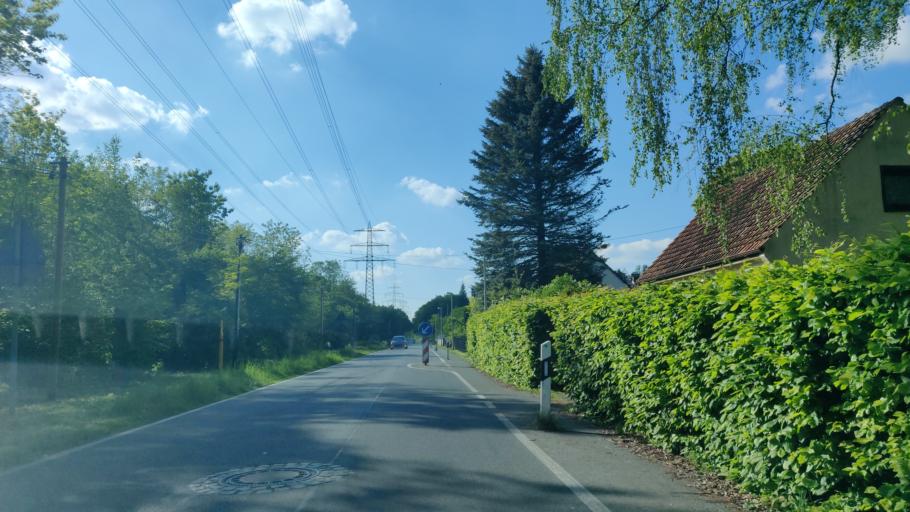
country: DE
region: Lower Saxony
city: Isernhagen Farster Bauerschaft
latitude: 52.4141
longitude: 9.8427
